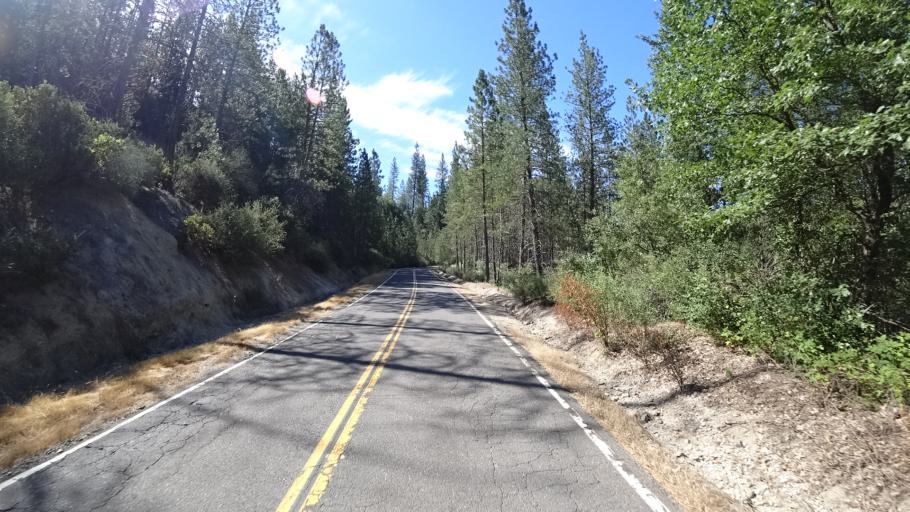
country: US
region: California
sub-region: Amador County
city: Pioneer
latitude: 38.3652
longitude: -120.5015
